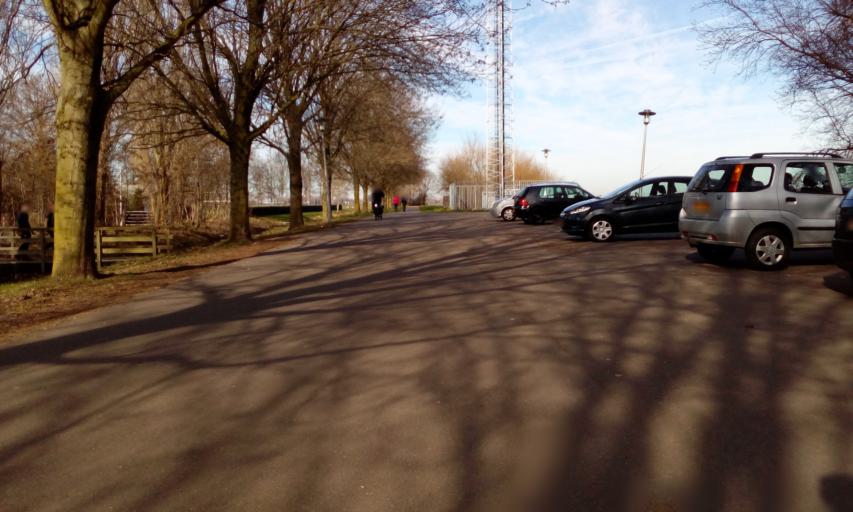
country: NL
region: South Holland
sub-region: Gemeente Rijnwoude
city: Benthuizen
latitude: 52.1009
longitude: 4.5964
